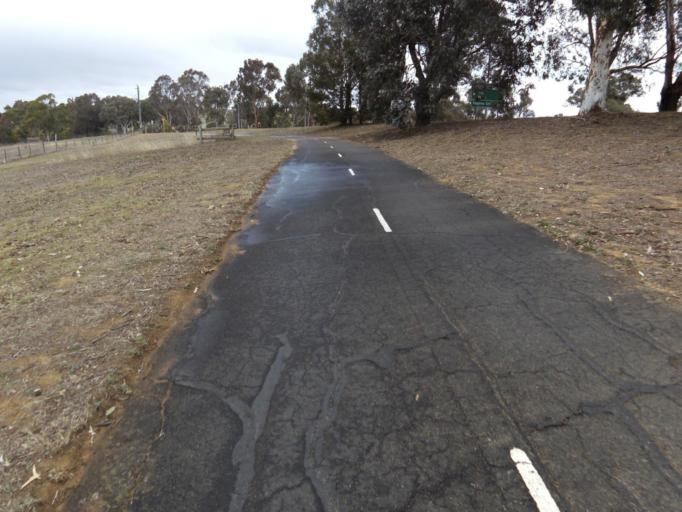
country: AU
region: Australian Capital Territory
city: Macquarie
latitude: -35.2751
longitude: 149.0761
